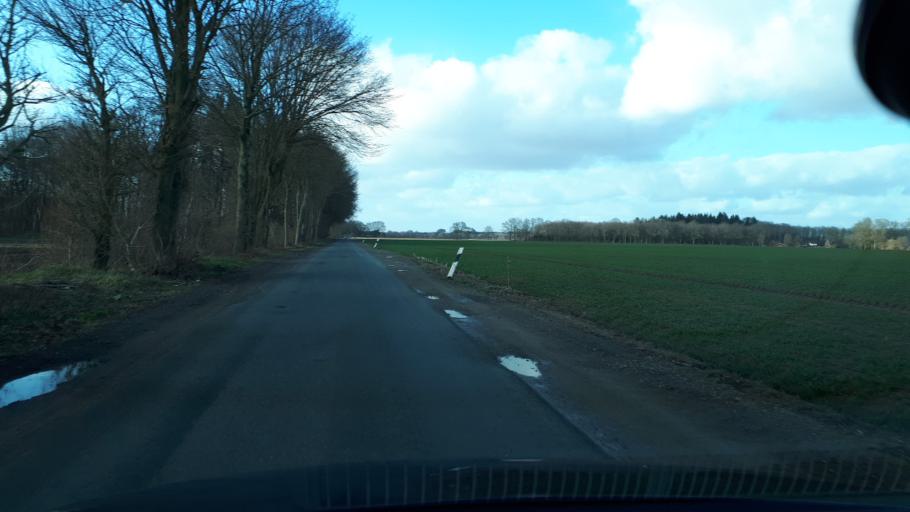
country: DE
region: Lower Saxony
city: Cloppenburg
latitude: 52.8367
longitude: 7.9979
